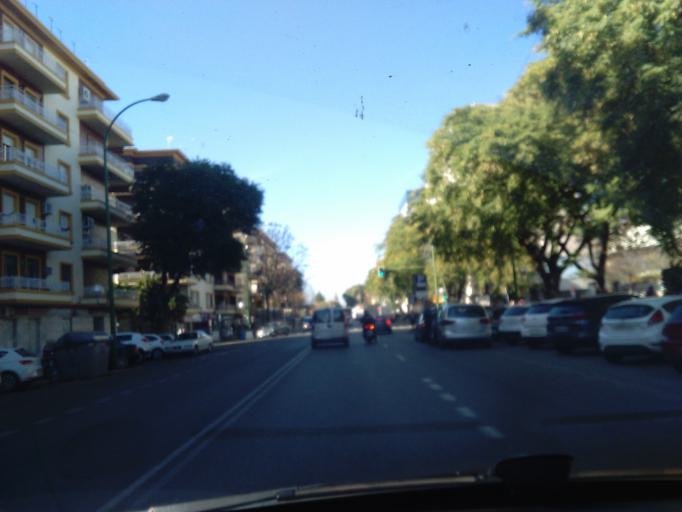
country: ES
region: Andalusia
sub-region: Provincia de Sevilla
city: Sevilla
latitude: 37.3825
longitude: -5.9709
